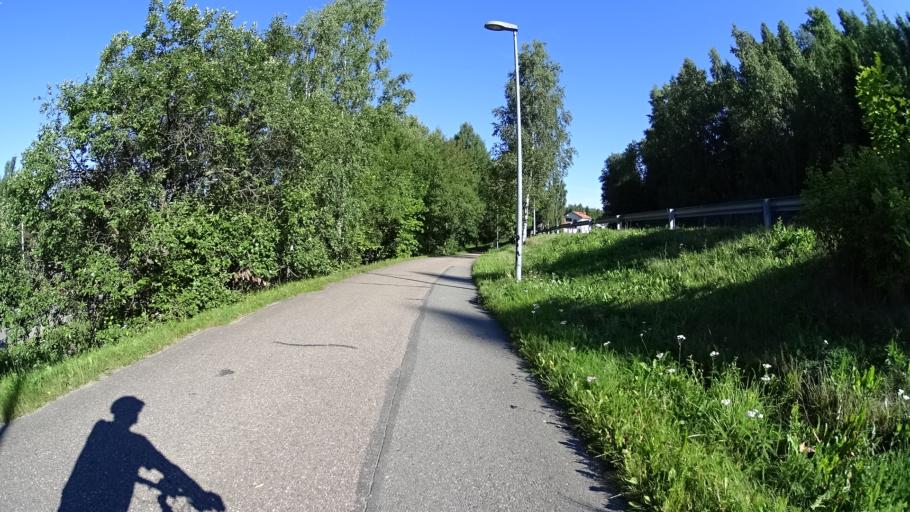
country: FI
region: Uusimaa
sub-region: Helsinki
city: Teekkarikylae
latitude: 60.2748
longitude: 24.8717
